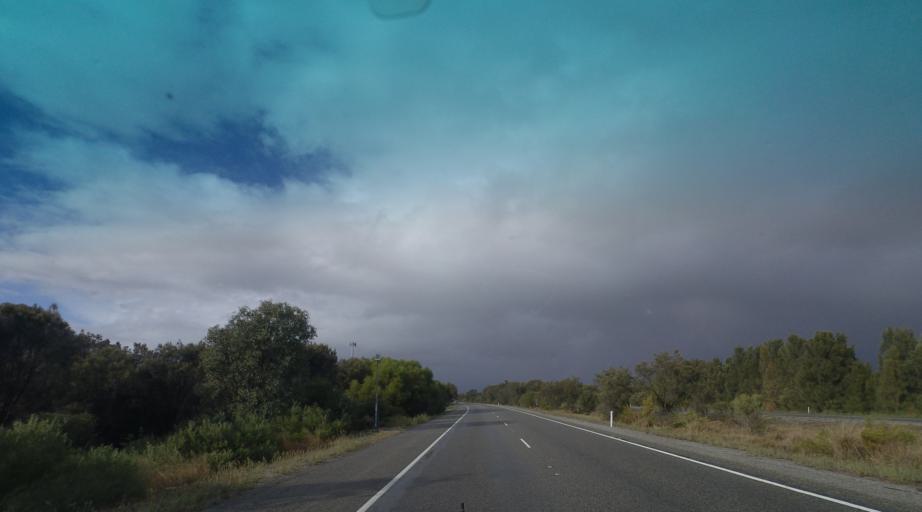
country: AU
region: Western Australia
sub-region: Serpentine-Jarrahdale
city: Oakford
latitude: -32.1949
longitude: 115.9625
